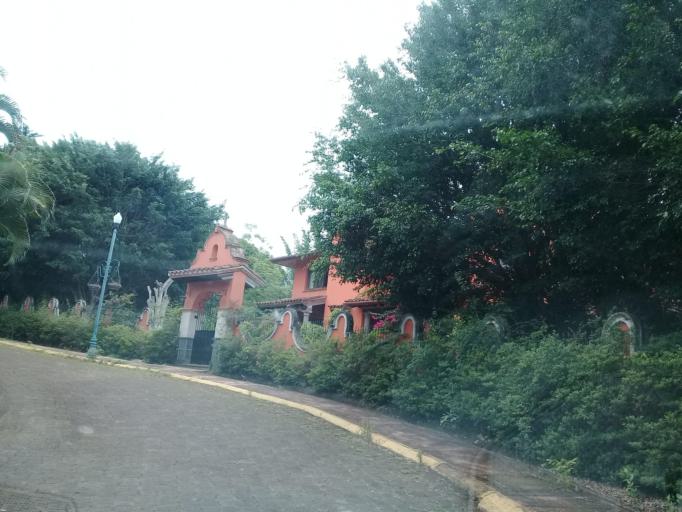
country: MX
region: Veracruz
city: El Castillo
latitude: 19.5260
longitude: -96.8760
